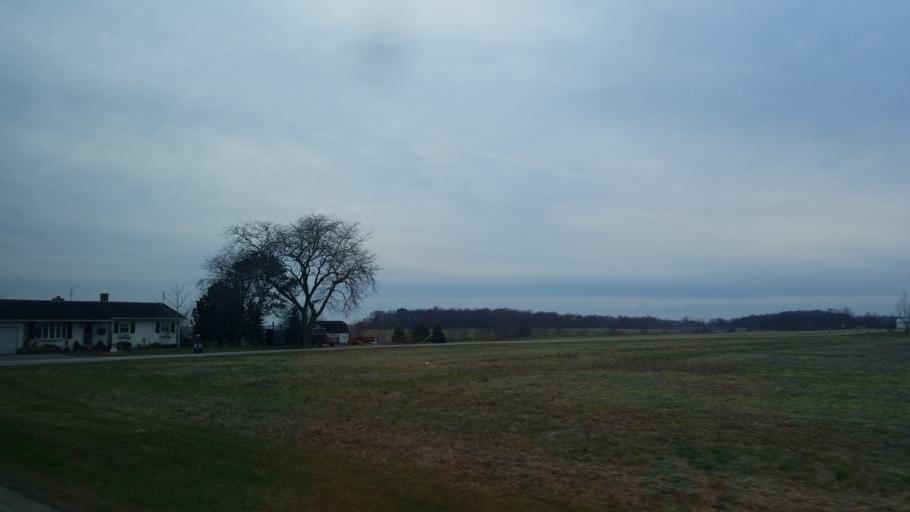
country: US
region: Indiana
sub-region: Adams County
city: Berne
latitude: 40.6955
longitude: -84.8792
